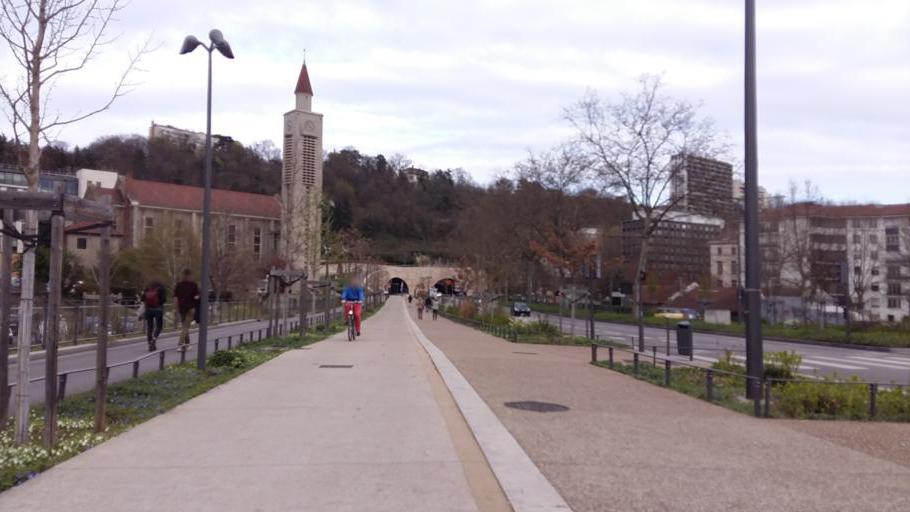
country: FR
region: Rhone-Alpes
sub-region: Departement du Rhone
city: Tassin-la-Demi-Lune
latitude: 45.7749
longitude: 4.8108
